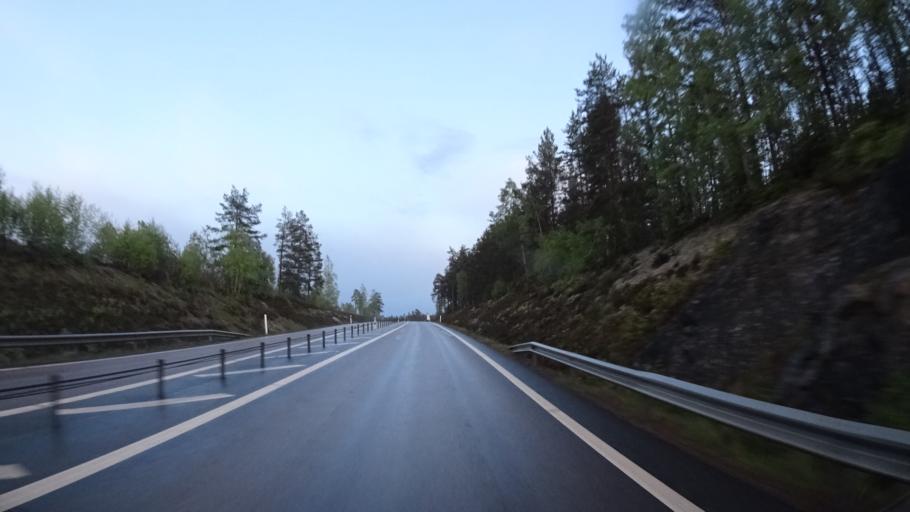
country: SE
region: Kalmar
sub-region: Vasterviks Kommun
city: Forserum
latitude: 58.0662
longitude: 16.5236
